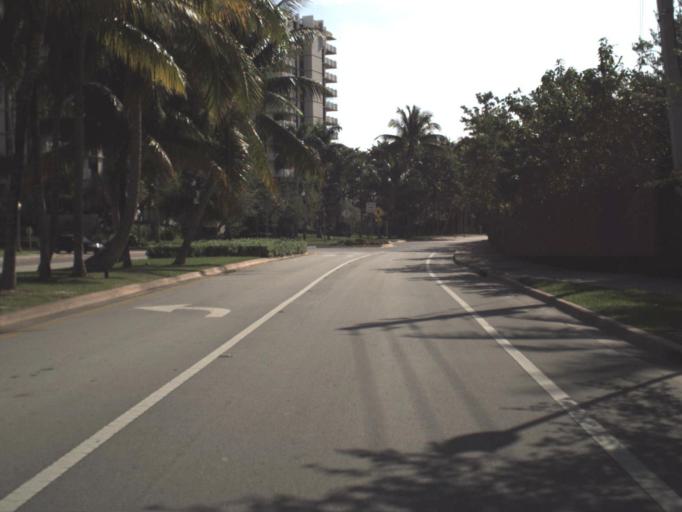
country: US
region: Florida
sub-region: Miami-Dade County
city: Key Biscayne
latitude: 25.6838
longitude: -80.1591
